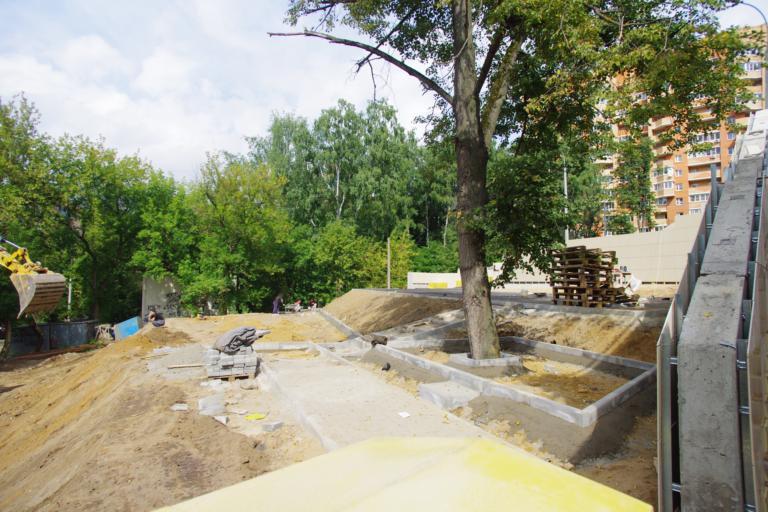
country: RU
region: Moskovskaya
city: Krasnogorsk
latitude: 55.8321
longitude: 37.3263
